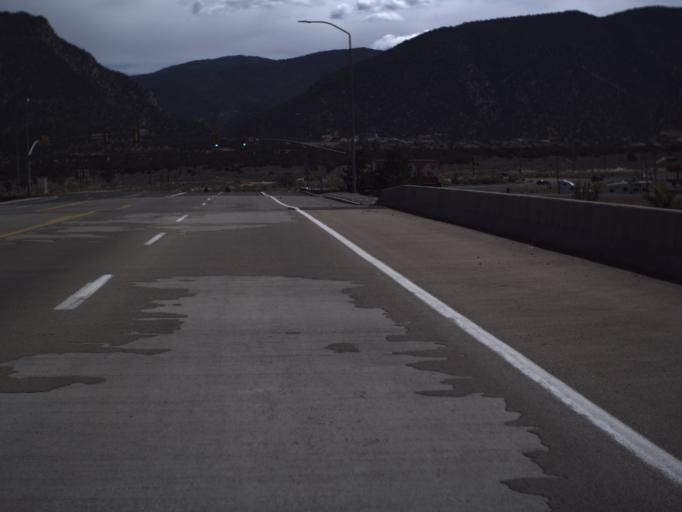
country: US
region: Utah
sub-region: Iron County
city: Cedar City
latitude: 37.7285
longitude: -113.0532
